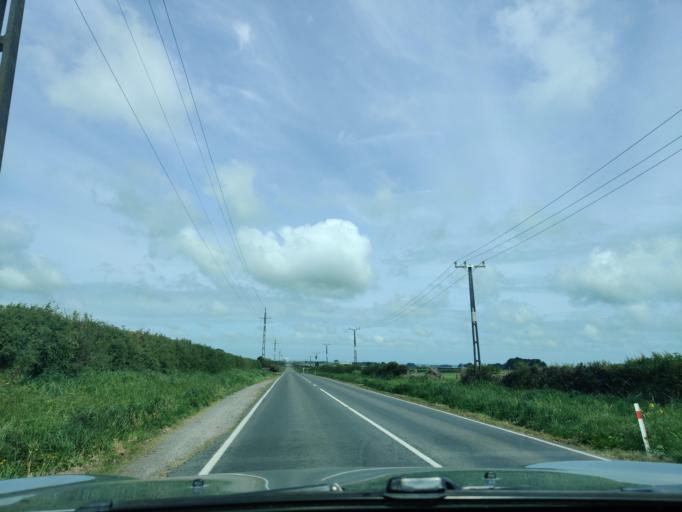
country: NZ
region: Taranaki
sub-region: South Taranaki District
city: Eltham
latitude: -39.4280
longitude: 174.1697
